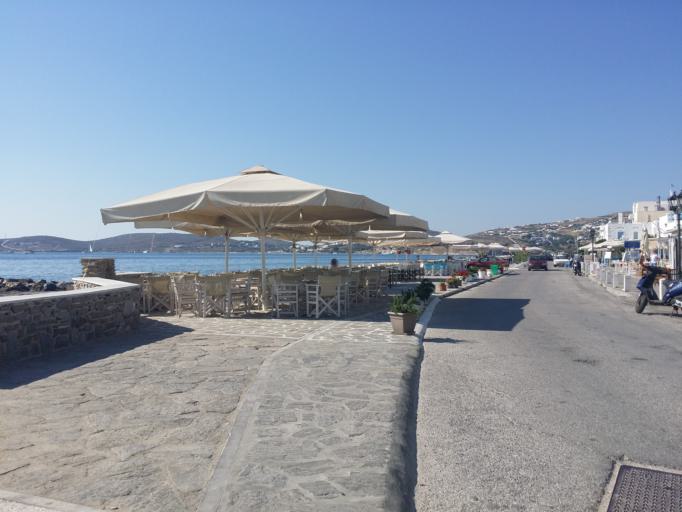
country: GR
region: South Aegean
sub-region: Nomos Kykladon
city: Paros
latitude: 37.0826
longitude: 25.1461
